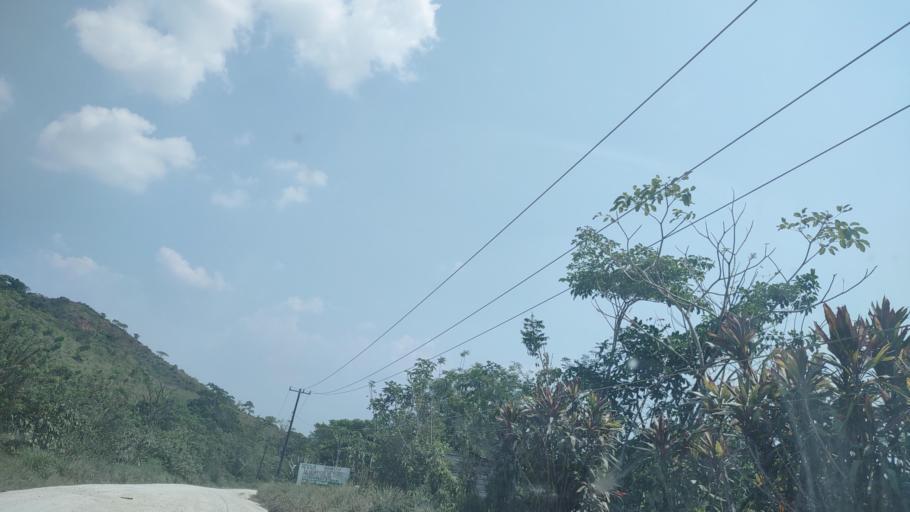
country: MX
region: Tabasco
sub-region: Huimanguillo
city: Francisco Rueda
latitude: 17.5695
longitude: -93.8866
